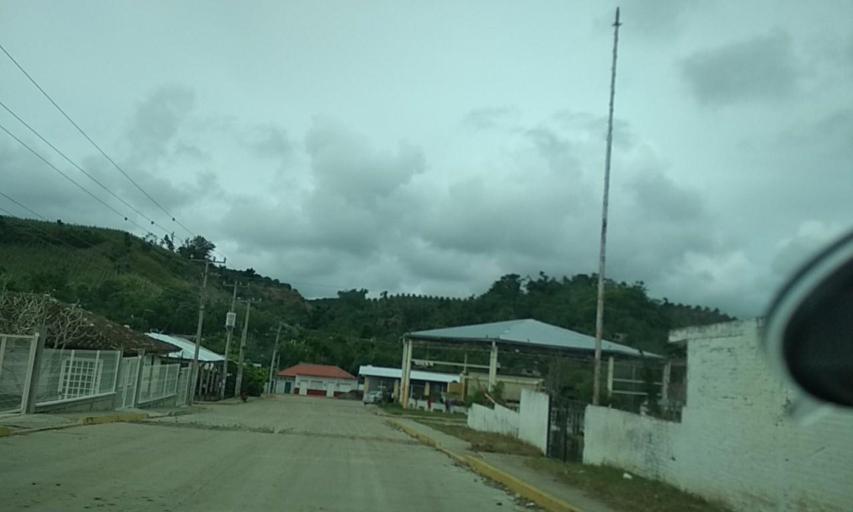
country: MX
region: Veracruz
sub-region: Papantla
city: Residencial Tajin
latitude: 20.6010
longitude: -97.3342
